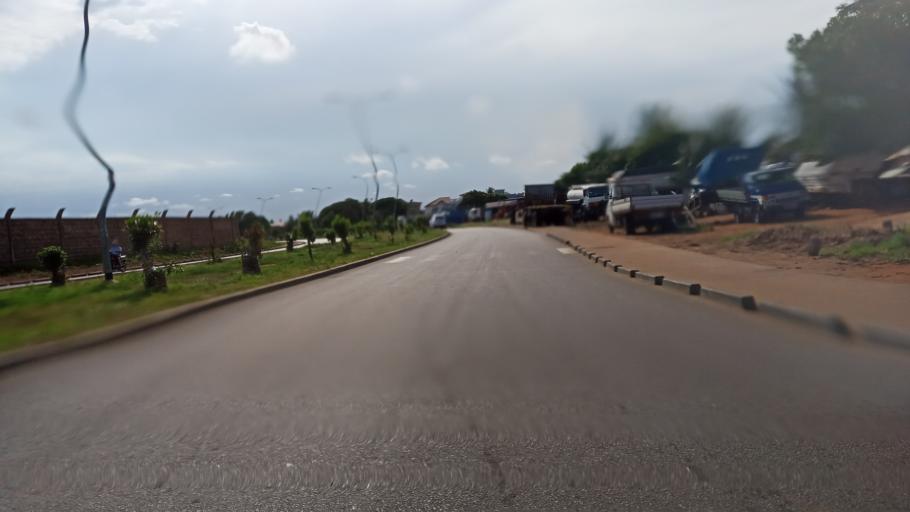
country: TG
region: Maritime
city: Lome
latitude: 6.1863
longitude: 1.2699
